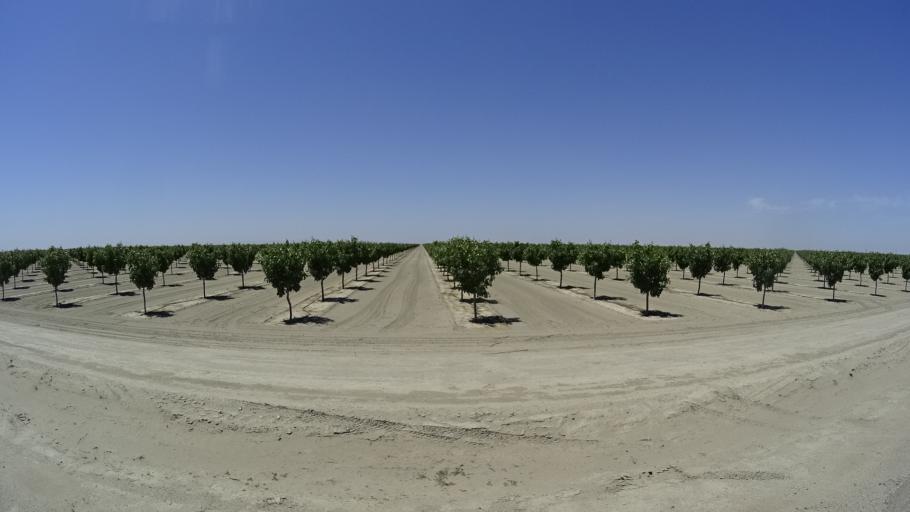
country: US
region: California
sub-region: Kings County
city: Corcoran
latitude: 36.1000
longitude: -119.5989
